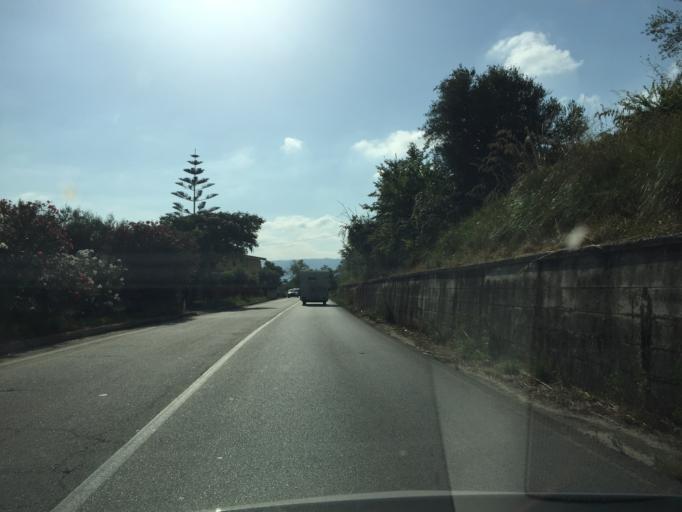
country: IT
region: Calabria
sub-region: Provincia di Vibo-Valentia
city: Pannaconi
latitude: 38.7165
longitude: 16.0551
